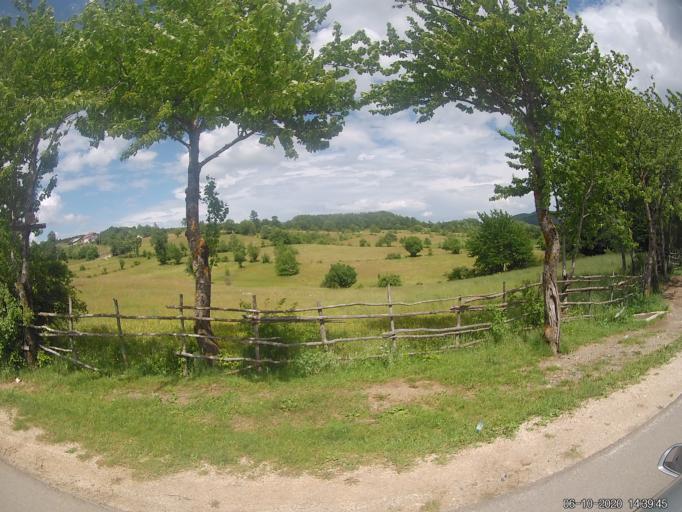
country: XK
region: Prizren
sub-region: Komuna e Therandes
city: Budakovo
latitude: 42.3991
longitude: 20.9449
